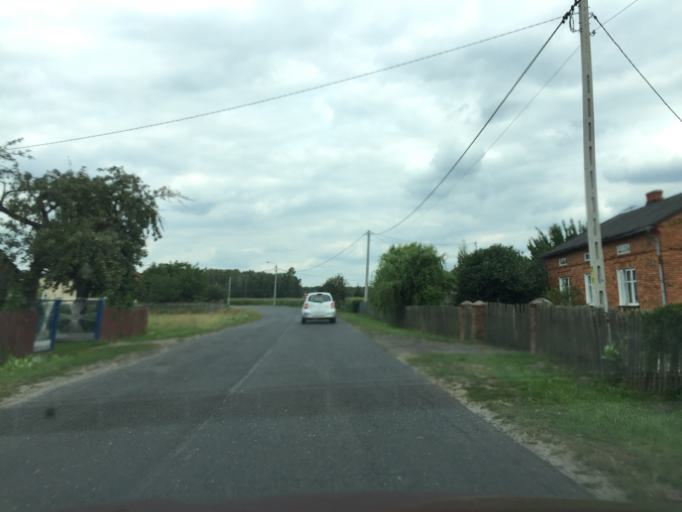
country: PL
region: Greater Poland Voivodeship
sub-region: Powiat kaliski
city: Stawiszyn
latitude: 51.9574
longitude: 18.1752
